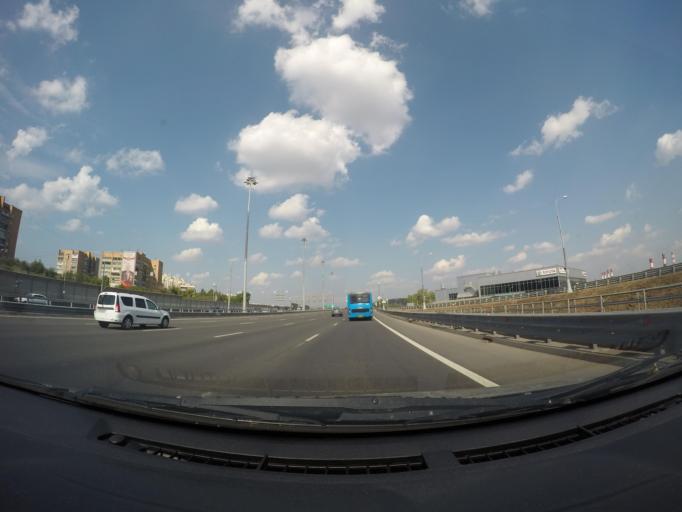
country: RU
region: Moskovskaya
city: Levoberezhnaya
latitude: 55.8886
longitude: 37.4836
